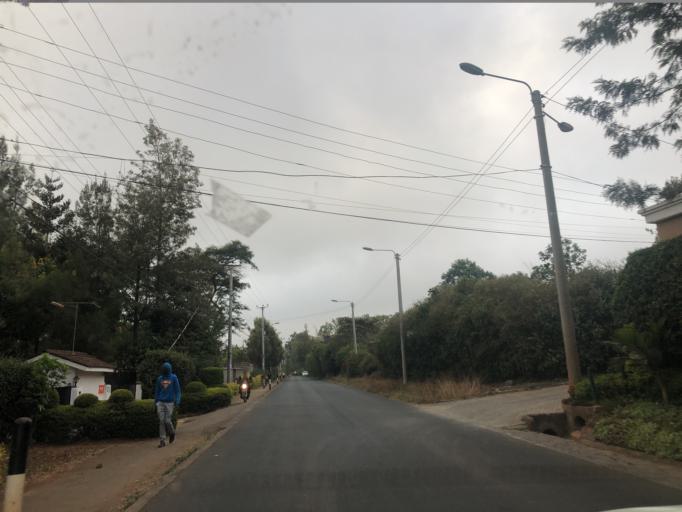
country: KE
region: Nairobi Area
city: Pumwani
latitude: -1.2297
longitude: 36.8571
